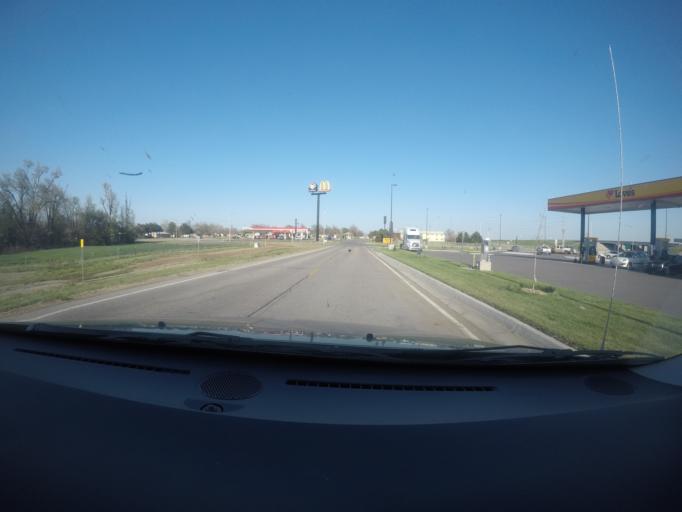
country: US
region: Kansas
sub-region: Reno County
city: South Hutchinson
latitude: 38.0146
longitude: -97.9414
